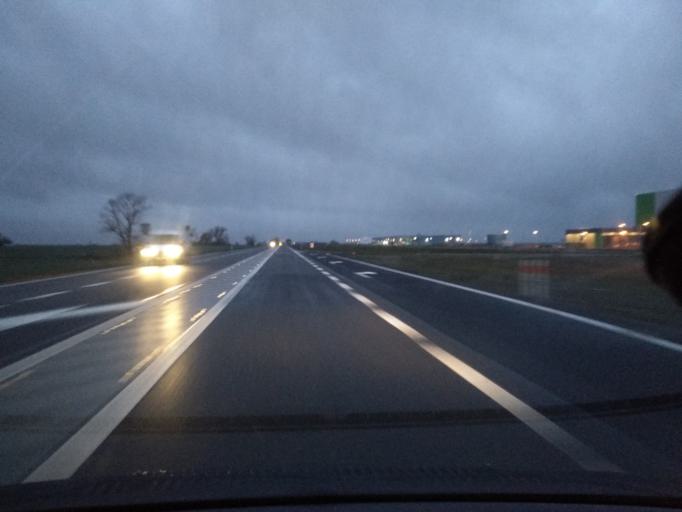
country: PL
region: Lower Silesian Voivodeship
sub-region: Powiat sredzki
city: Szczepanow
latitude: 51.1635
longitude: 16.6639
